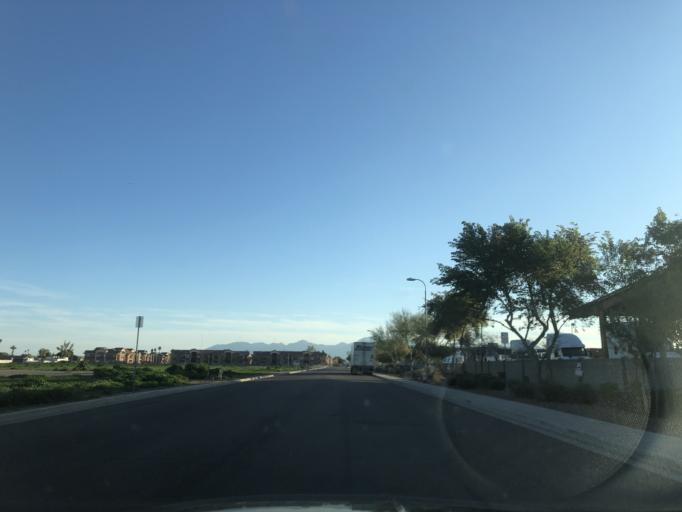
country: US
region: Arizona
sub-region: Maricopa County
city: Tolleson
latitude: 33.4571
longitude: -112.2681
